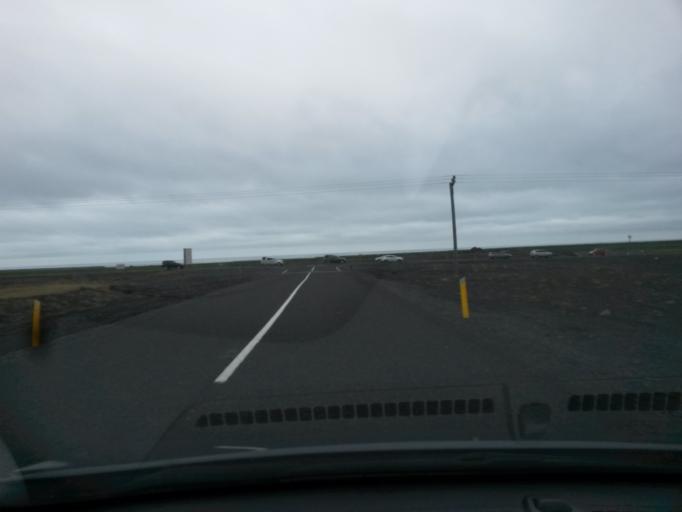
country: IS
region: South
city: Vestmannaeyjar
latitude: 63.4991
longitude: -19.3968
